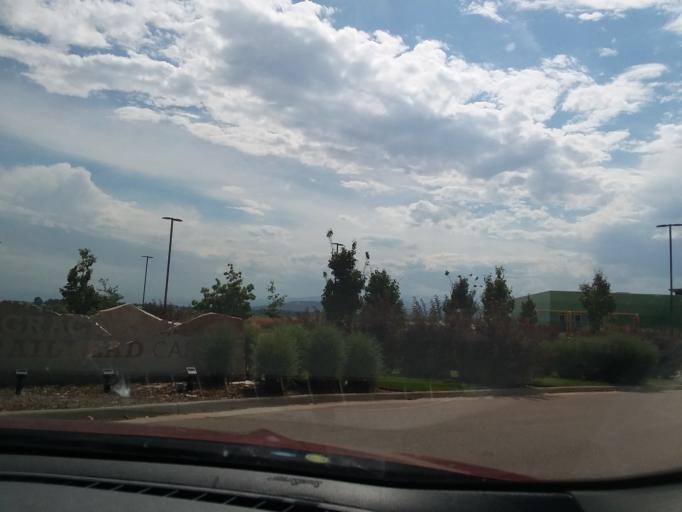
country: US
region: Colorado
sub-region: Larimer County
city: Berthoud
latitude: 40.3032
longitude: -105.1029
